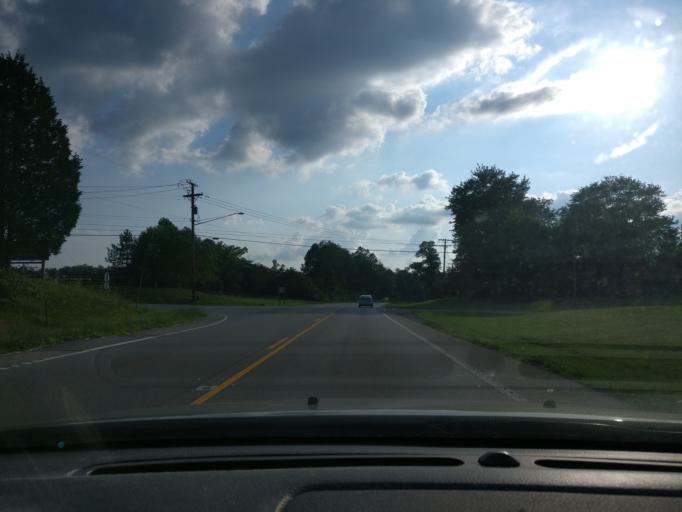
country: US
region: Ohio
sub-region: Warren County
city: Waynesville
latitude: 39.5189
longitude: -84.0722
